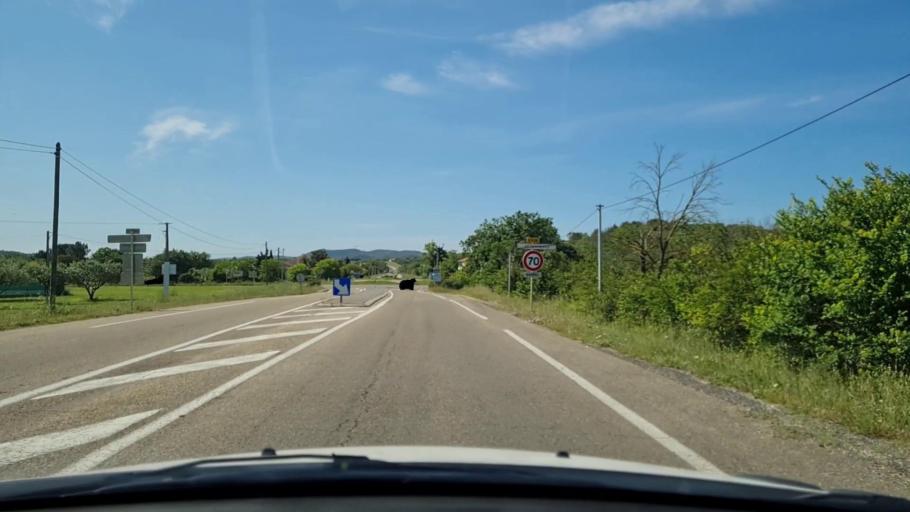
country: FR
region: Languedoc-Roussillon
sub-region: Departement du Gard
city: Vezenobres
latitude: 44.0441
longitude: 4.1456
